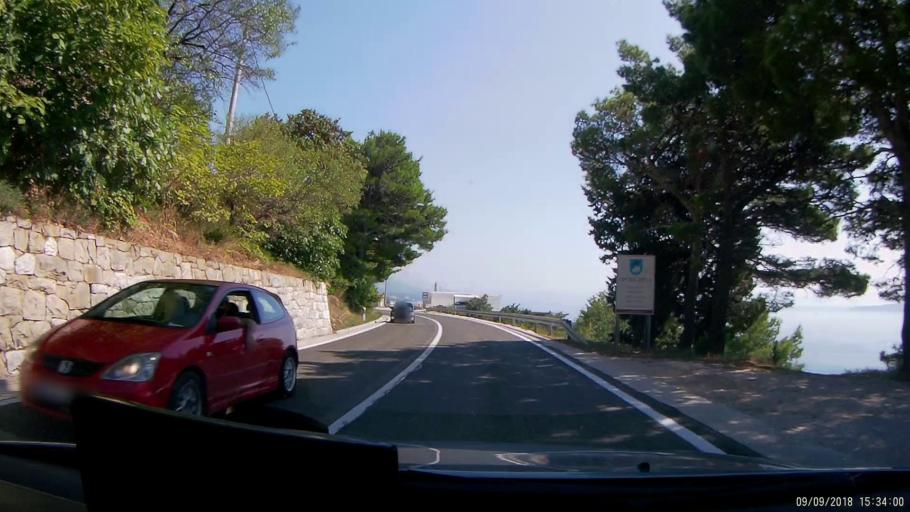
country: HR
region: Splitsko-Dalmatinska
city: Donja Brela
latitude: 43.3899
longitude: 16.9012
